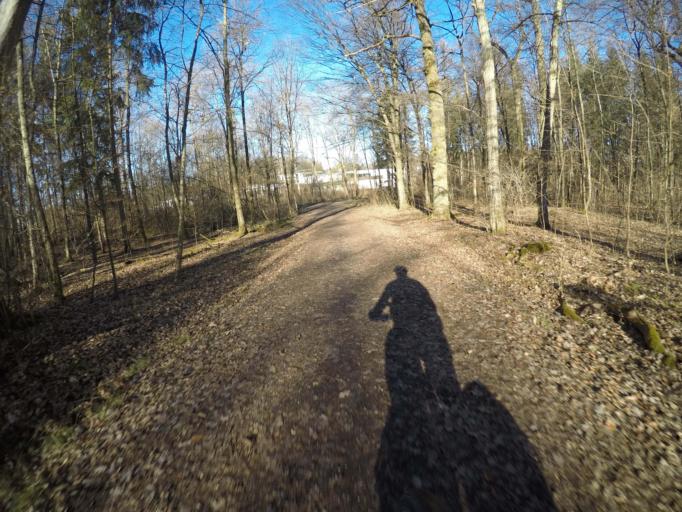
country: DE
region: Baden-Wuerttemberg
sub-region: Regierungsbezirk Stuttgart
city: Sindelfingen
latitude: 48.6929
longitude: 9.0293
